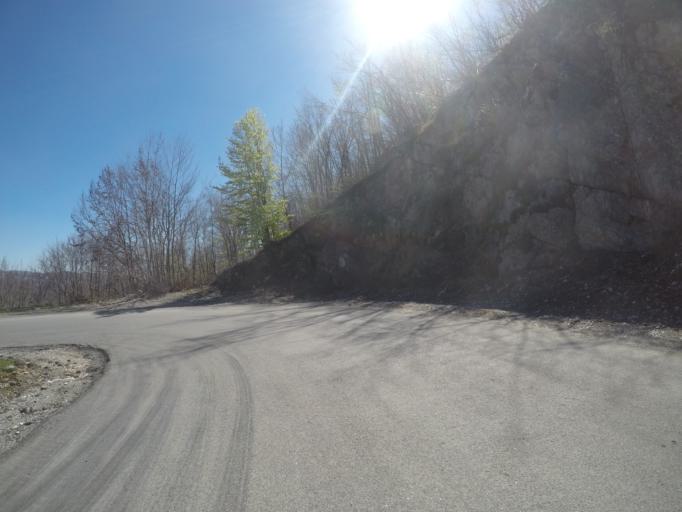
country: ME
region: Cetinje
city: Cetinje
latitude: 42.4342
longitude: 18.8676
